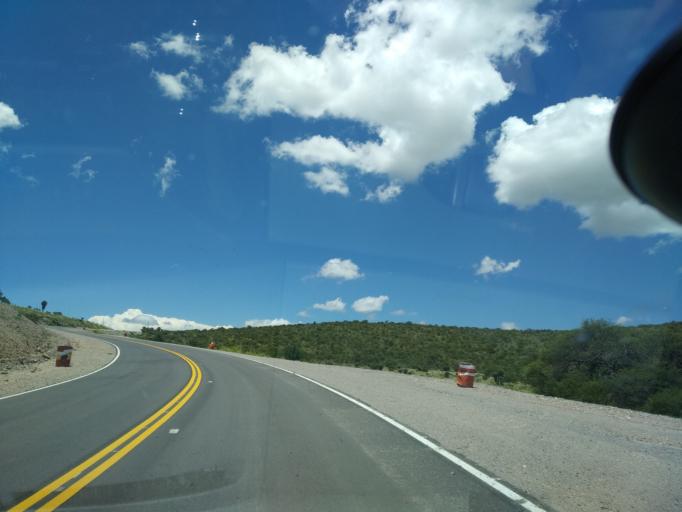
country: AR
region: Cordoba
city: Salsacate
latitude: -31.3753
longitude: -65.2860
